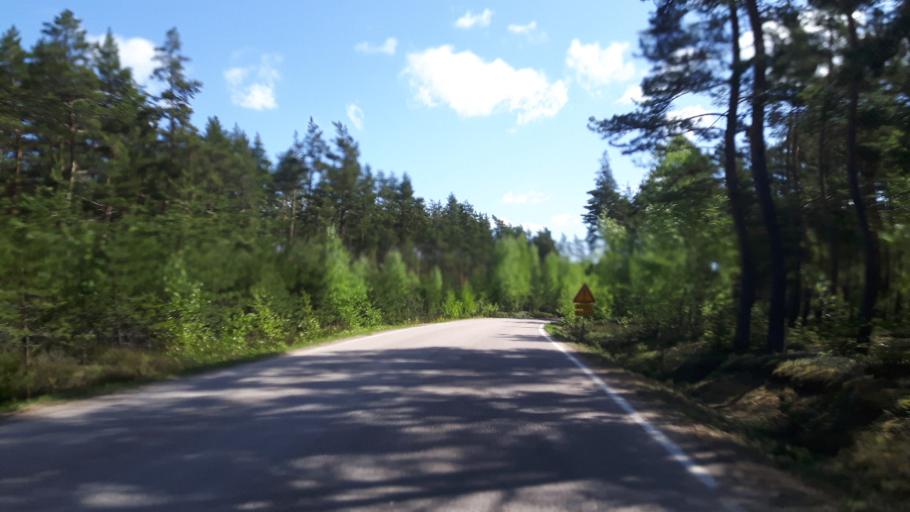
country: FI
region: Kymenlaakso
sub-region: Kotka-Hamina
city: Hamina
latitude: 60.5254
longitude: 27.2637
